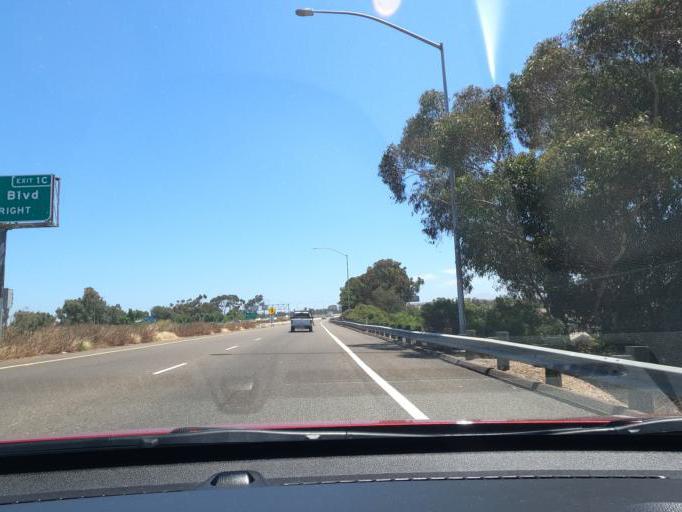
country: US
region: California
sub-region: San Diego County
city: Imperial Beach
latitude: 32.5664
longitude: -117.0698
